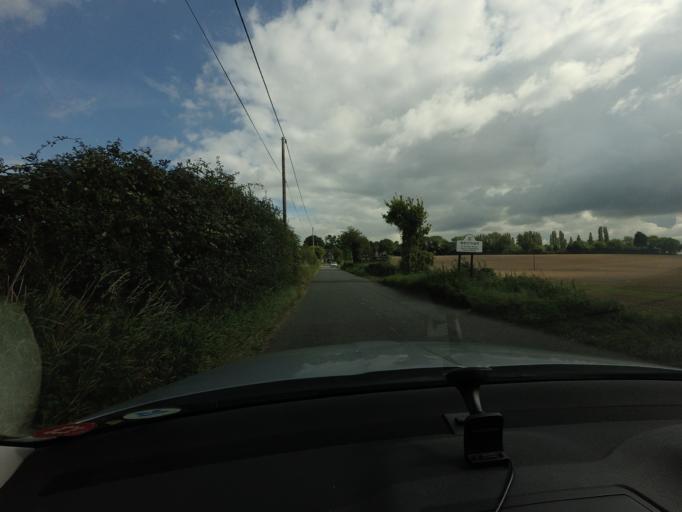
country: GB
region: England
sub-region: Kent
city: Borough Green
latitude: 51.3094
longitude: 0.3002
